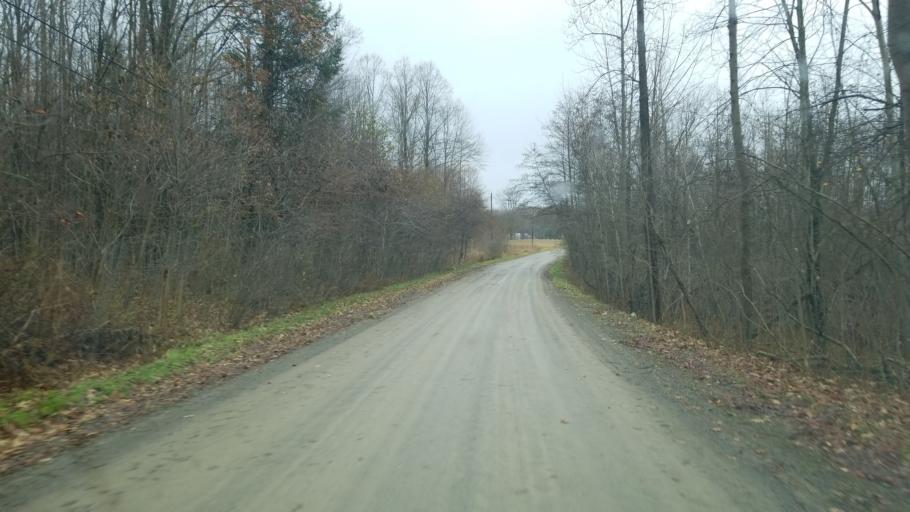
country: US
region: Ohio
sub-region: Ashtabula County
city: Conneaut
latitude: 41.8992
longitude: -80.5977
